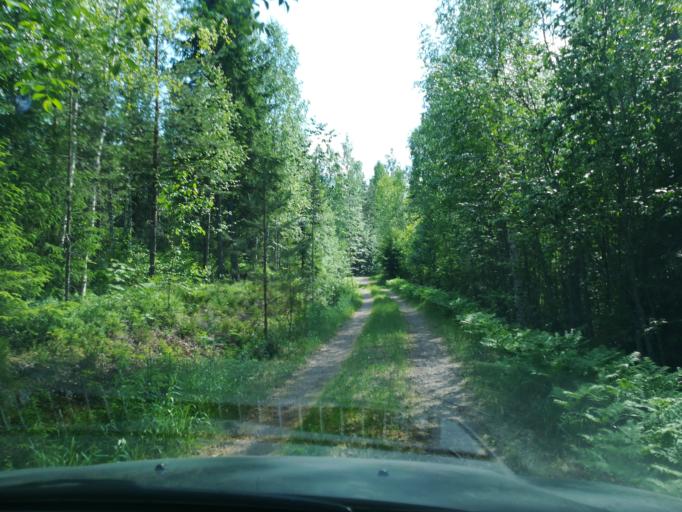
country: FI
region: South Karelia
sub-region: Imatra
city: Ruokolahti
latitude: 61.4826
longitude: 28.8709
